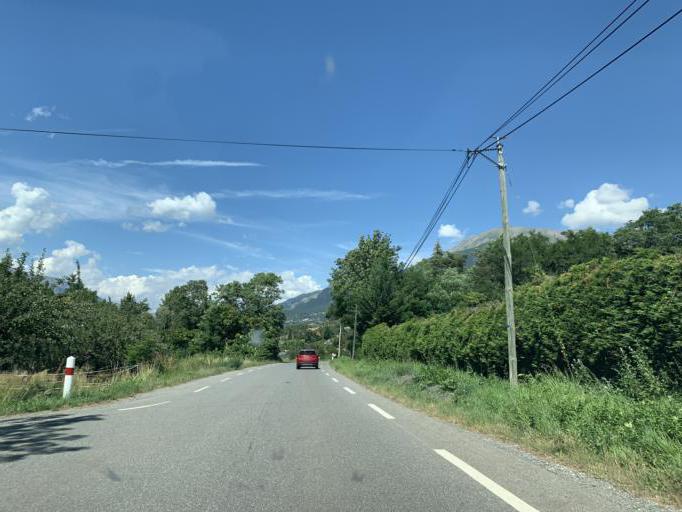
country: FR
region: Provence-Alpes-Cote d'Azur
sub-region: Departement des Hautes-Alpes
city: Embrun
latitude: 44.5458
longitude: 6.4987
